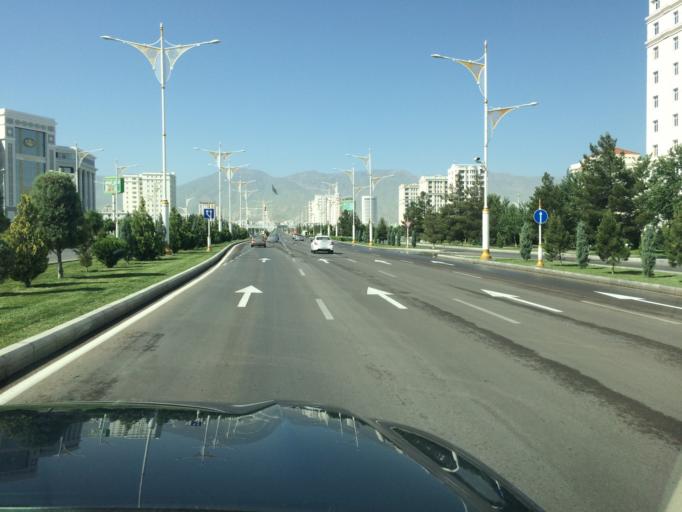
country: TM
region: Ahal
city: Ashgabat
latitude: 37.9000
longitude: 58.3620
